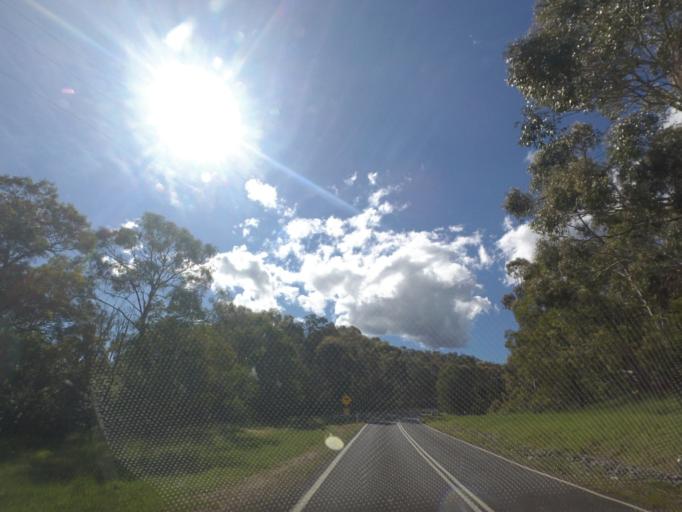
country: AU
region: Victoria
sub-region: Moorabool
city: Bacchus Marsh
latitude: -37.5545
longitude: 144.3010
